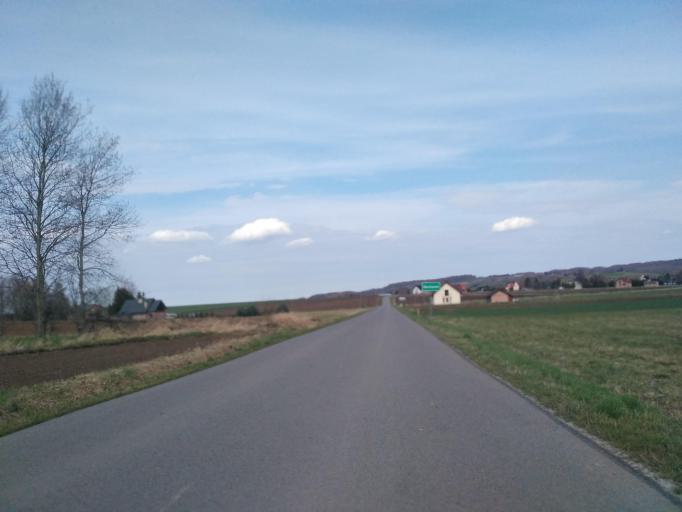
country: PL
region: Subcarpathian Voivodeship
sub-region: Powiat ropczycko-sedziszowski
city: Iwierzyce
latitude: 50.0115
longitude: 21.7882
